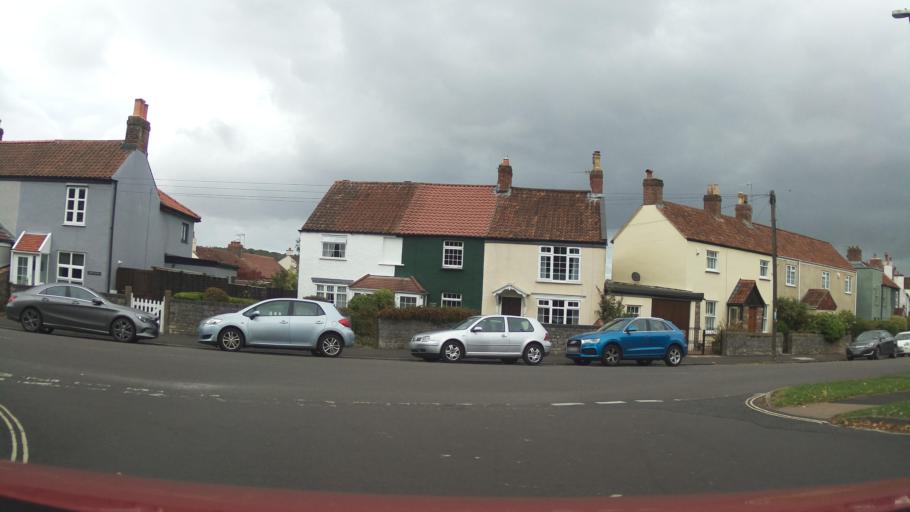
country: GB
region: England
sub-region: Bristol
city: Bristol
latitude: 51.4889
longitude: -2.6234
